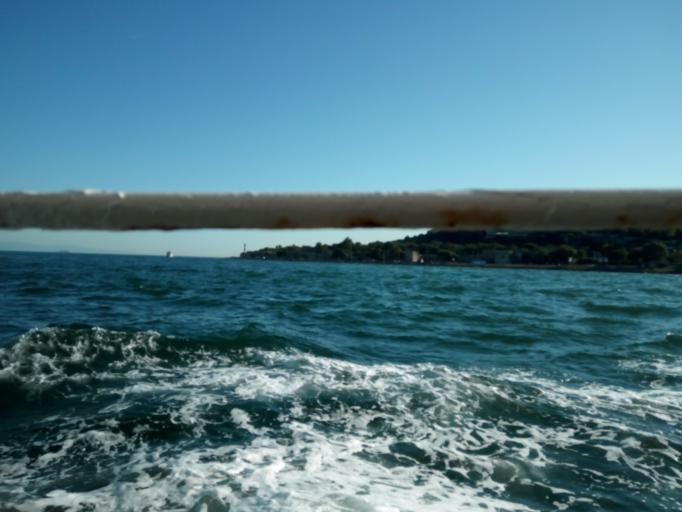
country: TR
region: Istanbul
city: Eminoenue
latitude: 41.0171
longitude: 28.9915
